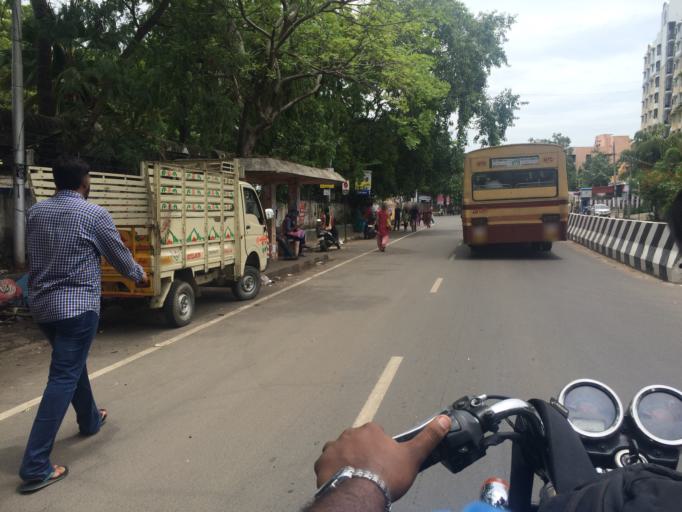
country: IN
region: Tamil Nadu
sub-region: Kancheepuram
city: Alandur
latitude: 12.9910
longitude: 80.2200
